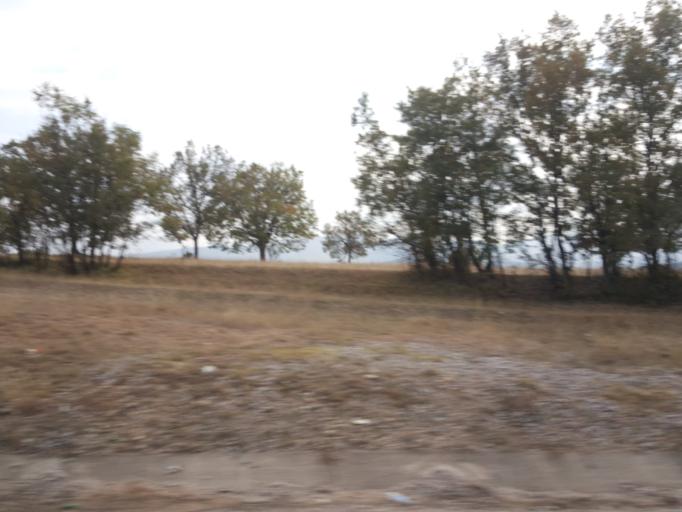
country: TR
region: Sinop
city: Sarayduzu
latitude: 41.3337
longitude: 34.7796
